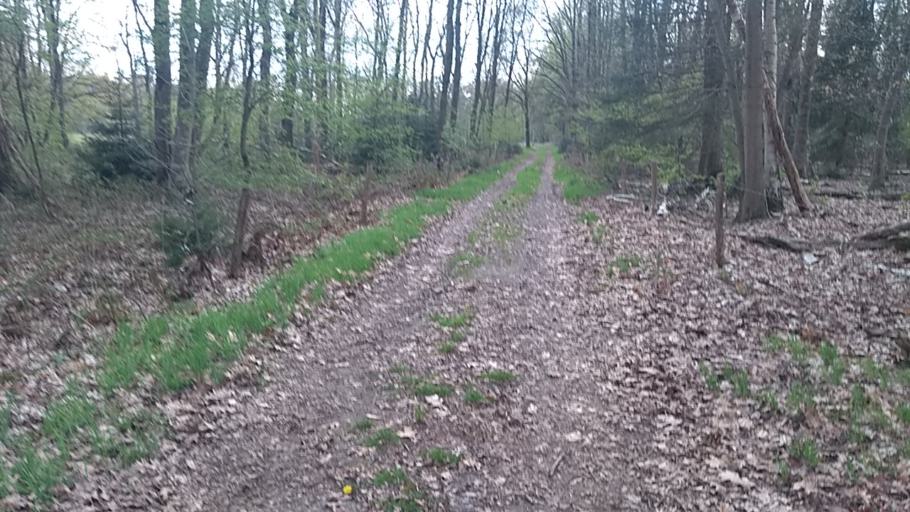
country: NL
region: Limburg
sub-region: Gemeente Leudal
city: Heythuysen
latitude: 51.2962
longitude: 5.8679
